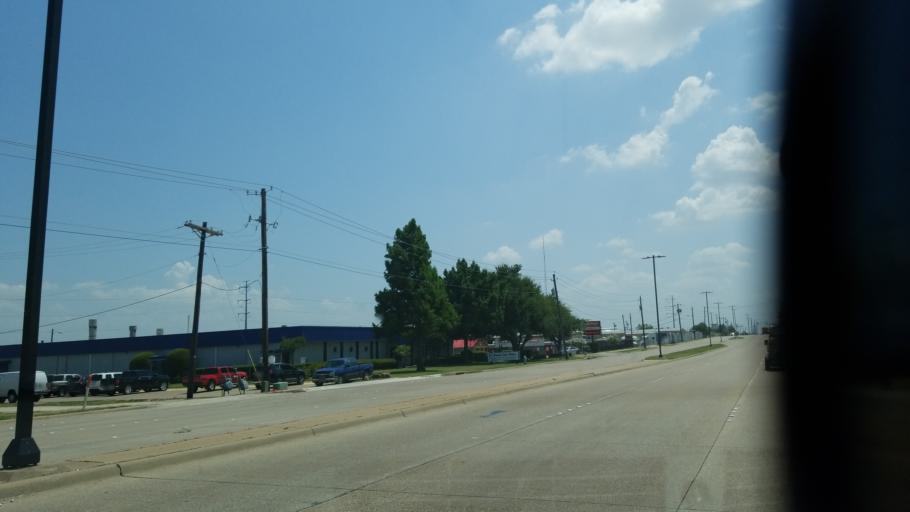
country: US
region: Texas
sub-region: Dallas County
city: Garland
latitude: 32.9264
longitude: -96.6308
